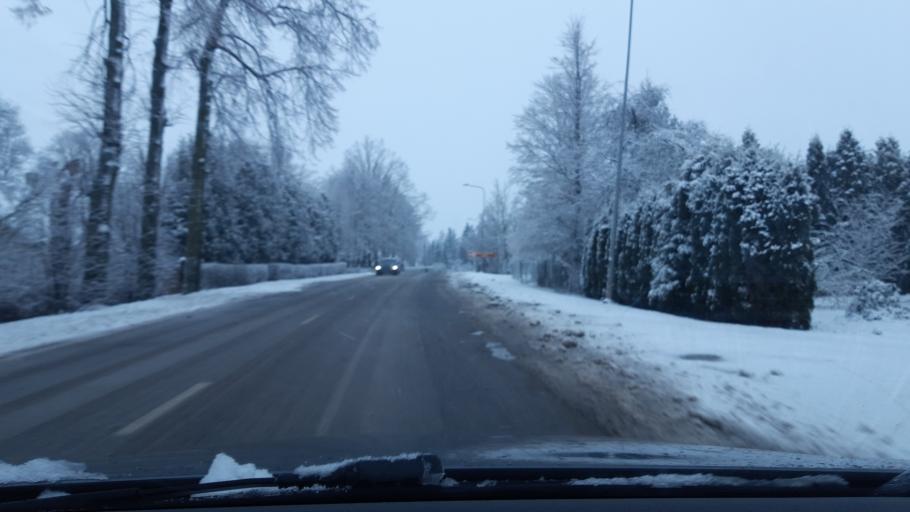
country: LT
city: Kaisiadorys
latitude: 54.8472
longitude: 24.3418
